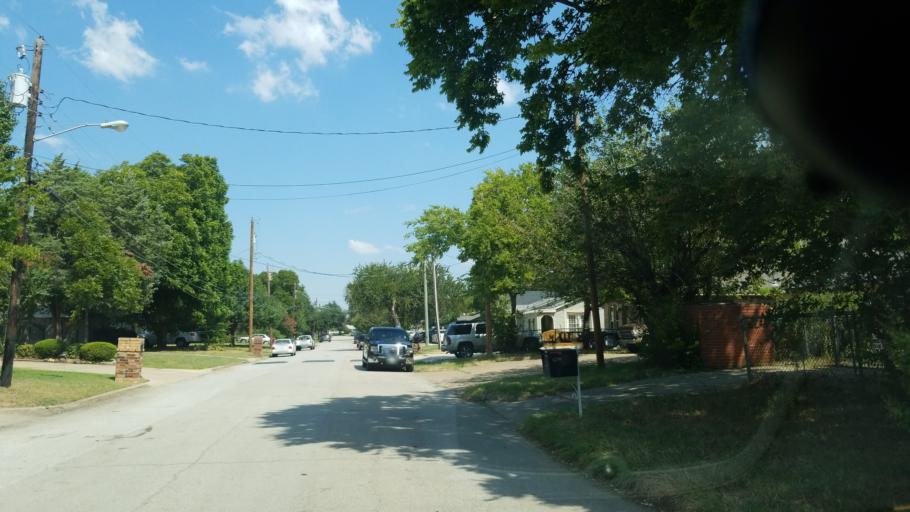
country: US
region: Texas
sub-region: Dallas County
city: Grand Prairie
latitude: 32.7125
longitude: -96.9891
